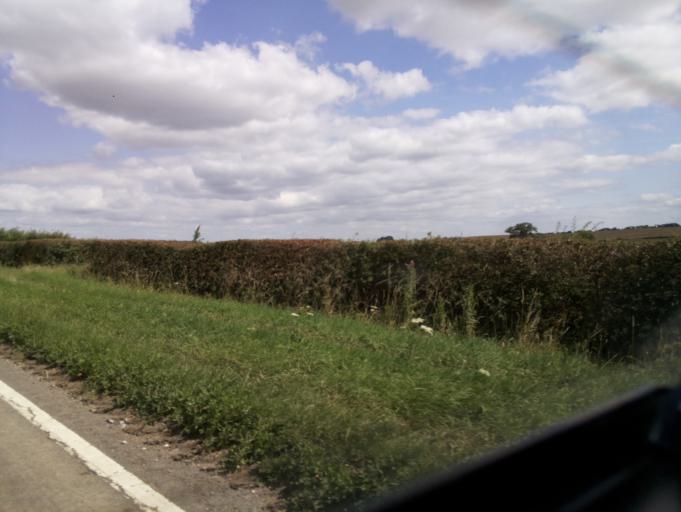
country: GB
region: England
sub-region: Buckinghamshire
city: Winslow
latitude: 51.9021
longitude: -0.8340
